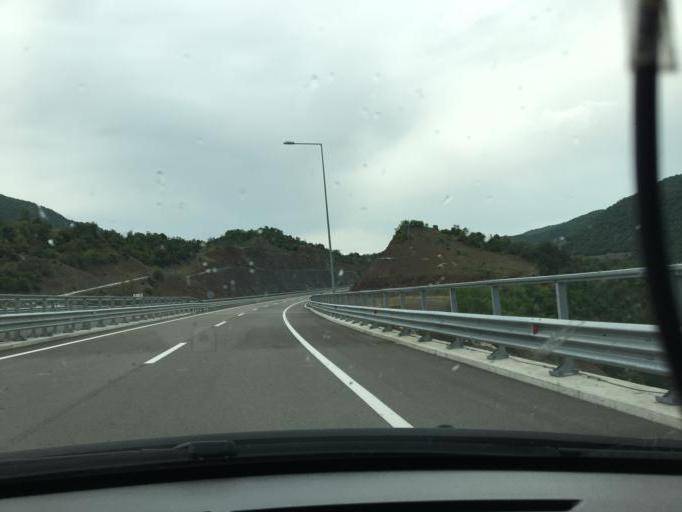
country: MK
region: Demir Kapija
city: Demir Kapija
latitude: 41.3700
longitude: 22.3393
